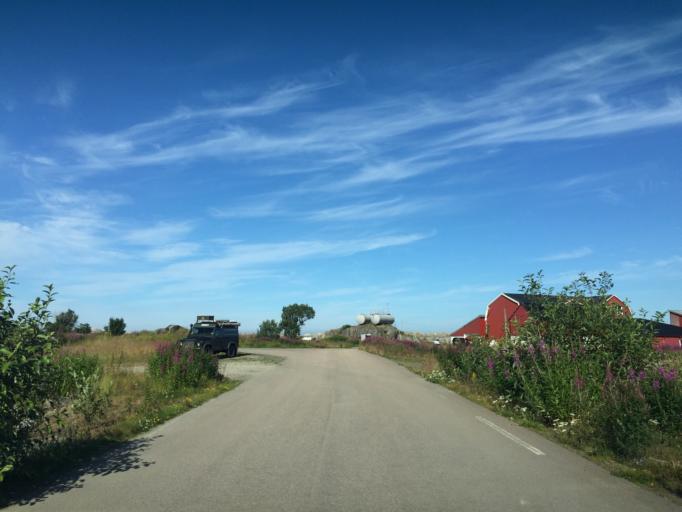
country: NO
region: Nordland
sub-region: Vagan
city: Kabelvag
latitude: 68.3855
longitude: 14.4106
